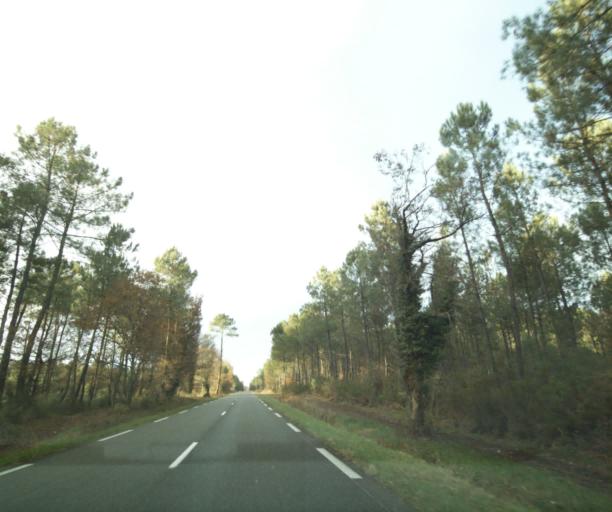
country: FR
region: Aquitaine
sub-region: Departement des Landes
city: Gabarret
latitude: 44.0378
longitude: -0.0338
